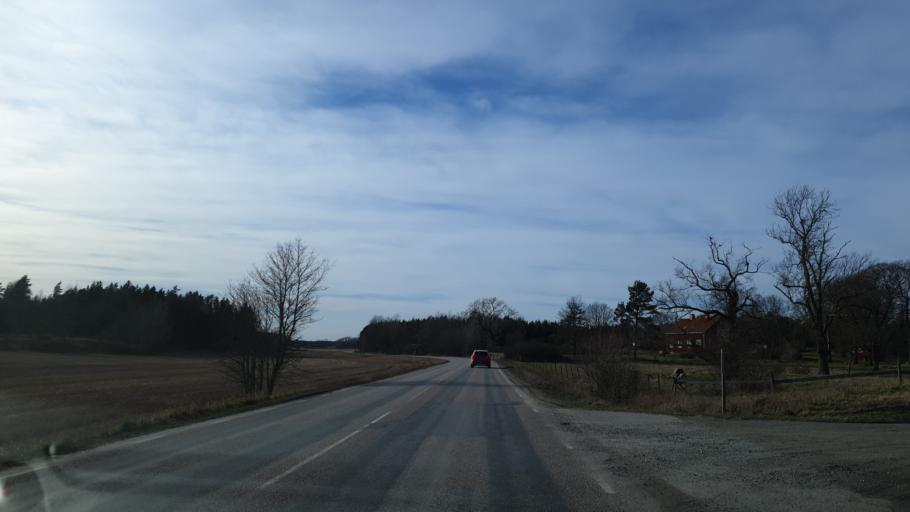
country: SE
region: Uppsala
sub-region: Enkopings Kommun
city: Grillby
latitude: 59.5959
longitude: 17.1750
